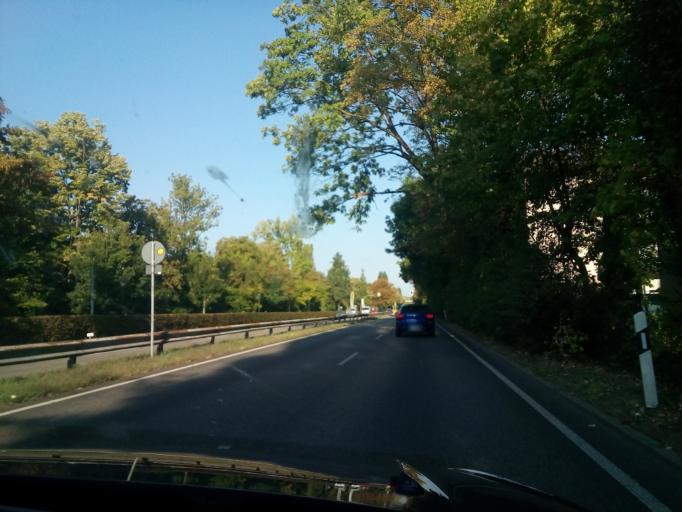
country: DE
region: Baden-Wuerttemberg
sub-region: Karlsruhe Region
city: Baden-Baden
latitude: 48.7779
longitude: 8.2141
